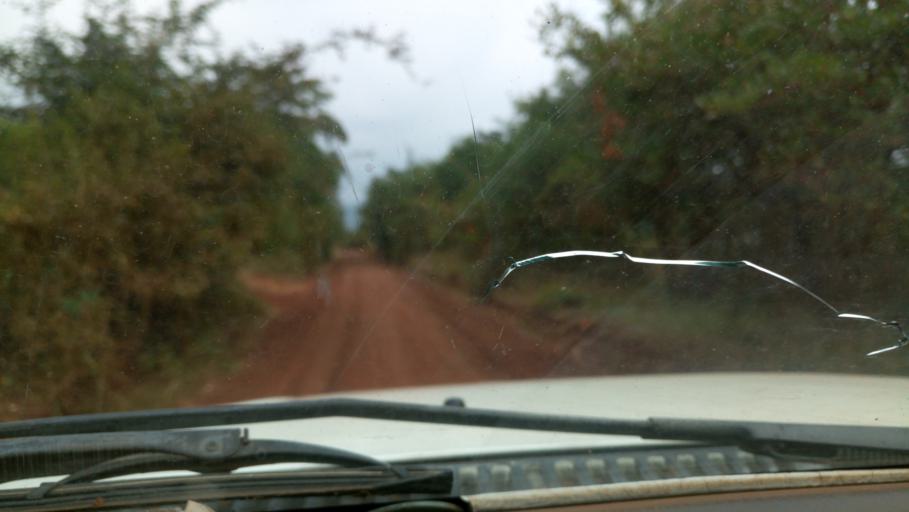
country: KE
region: Murang'a District
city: Maragua
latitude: -0.7830
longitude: 37.2072
